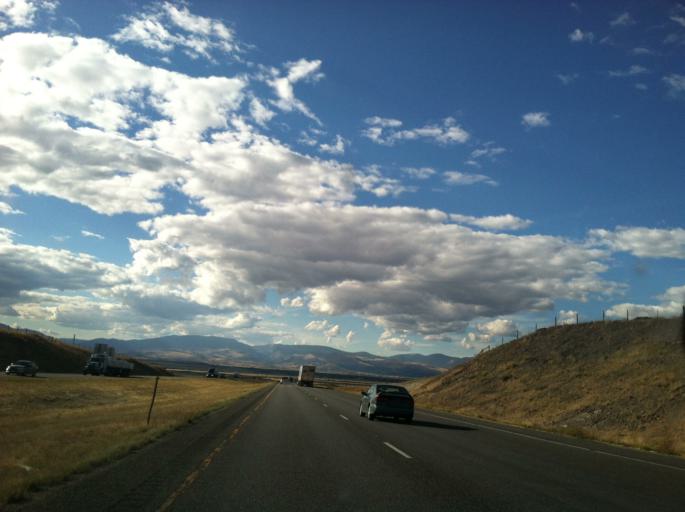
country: US
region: Montana
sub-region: Deer Lodge County
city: Warm Springs
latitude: 46.0571
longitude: -112.7617
